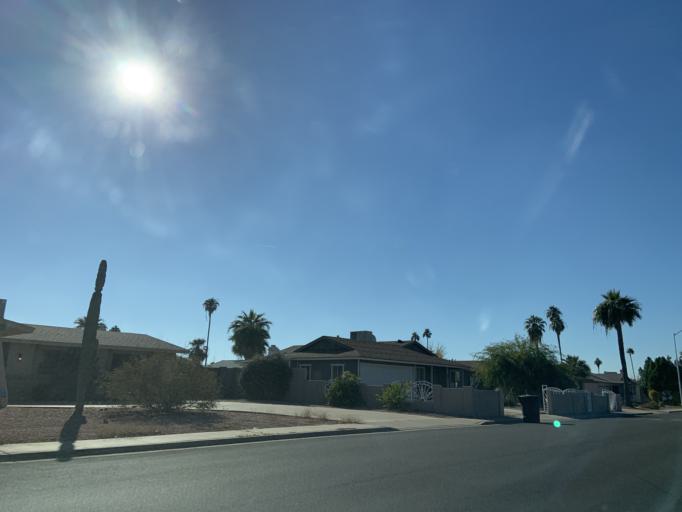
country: US
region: Arizona
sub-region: Maricopa County
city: Tempe
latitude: 33.3996
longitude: -111.8774
